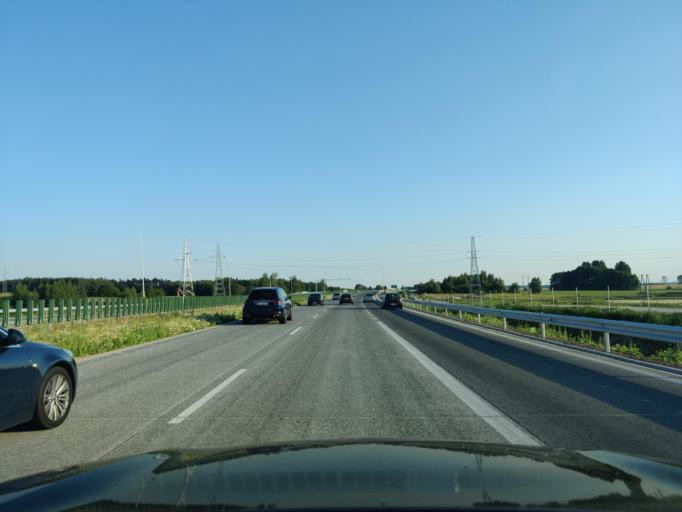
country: PL
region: Masovian Voivodeship
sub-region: Powiat mlawski
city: Mlawa
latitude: 53.0971
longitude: 20.4121
